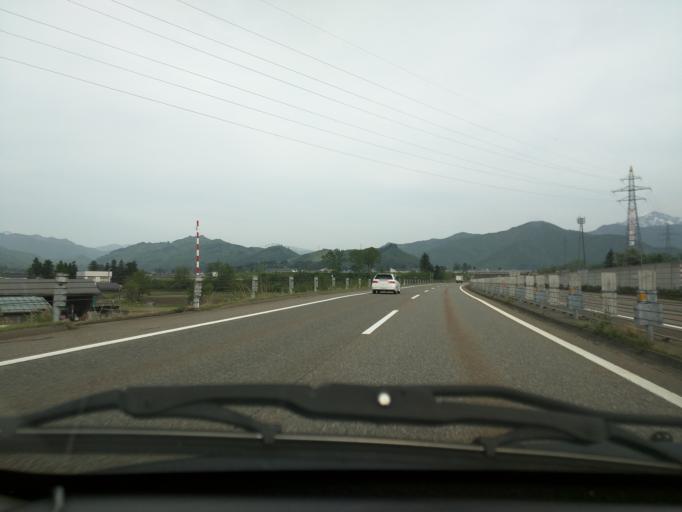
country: JP
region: Niigata
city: Ojiya
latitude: 37.2408
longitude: 138.9674
